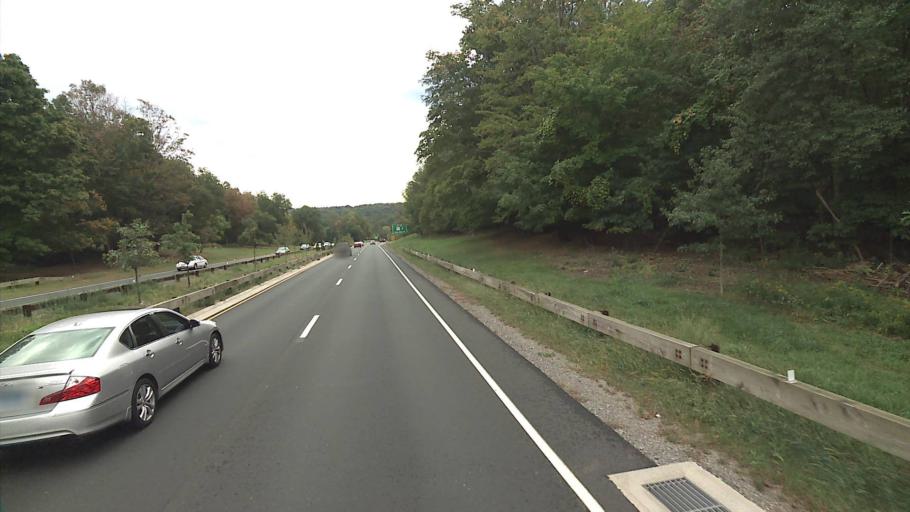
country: US
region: Connecticut
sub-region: Fairfield County
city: North Stamford
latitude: 41.1012
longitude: -73.5728
